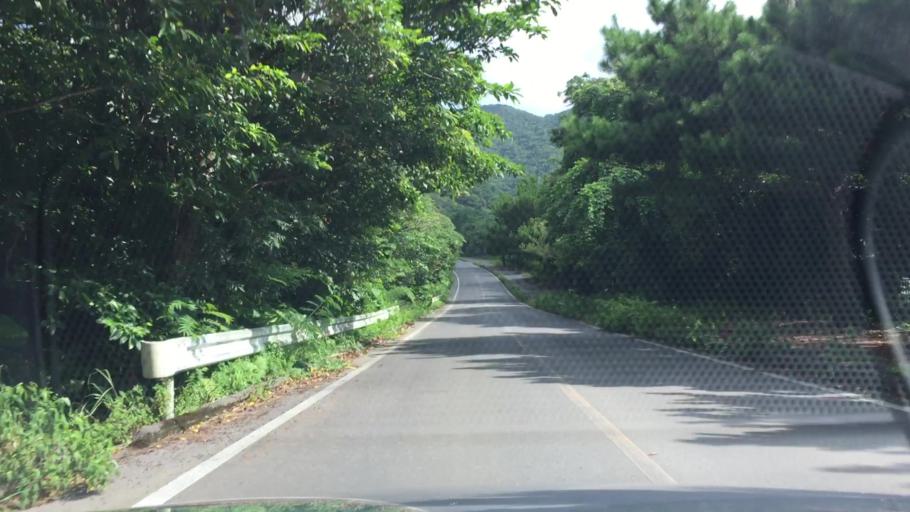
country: JP
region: Okinawa
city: Ishigaki
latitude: 24.4279
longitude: 124.2107
